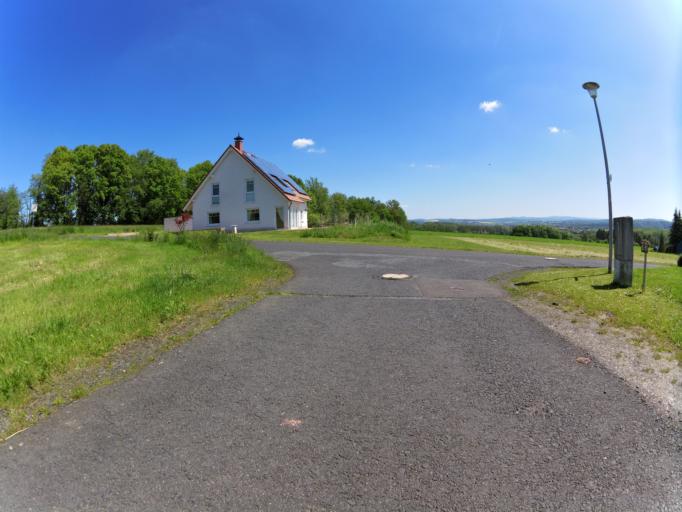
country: DE
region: Thuringia
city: Dankmarshausen
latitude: 50.9540
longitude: 9.9999
